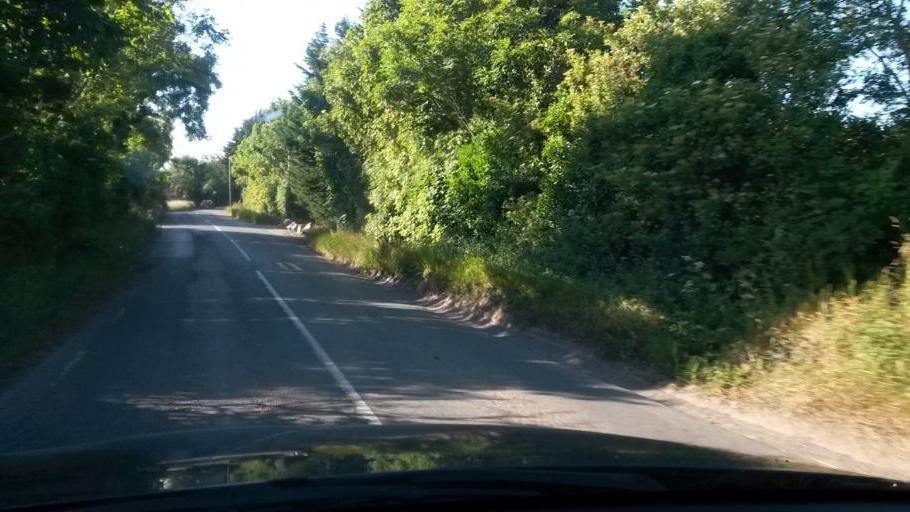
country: IE
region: Leinster
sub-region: Dublin City
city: Finglas
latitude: 53.4510
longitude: -6.3085
